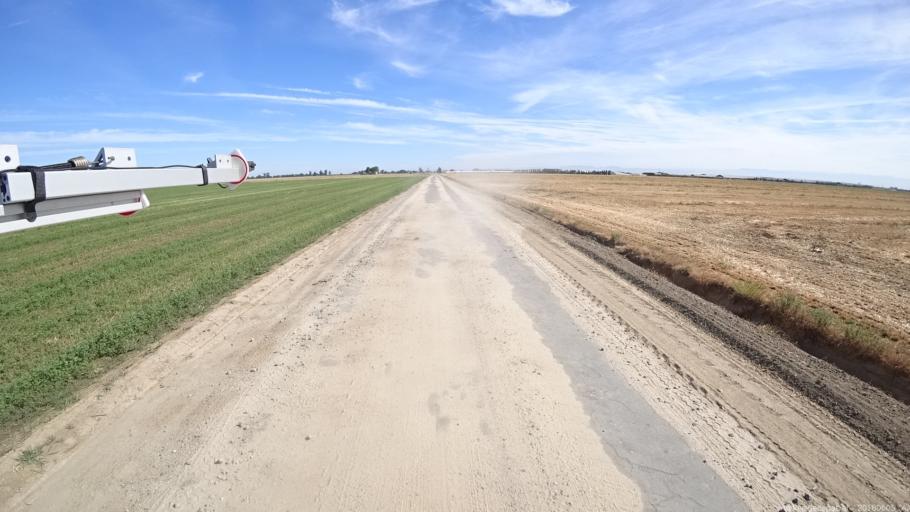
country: US
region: California
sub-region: Madera County
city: Chowchilla
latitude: 37.1291
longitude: -120.2927
